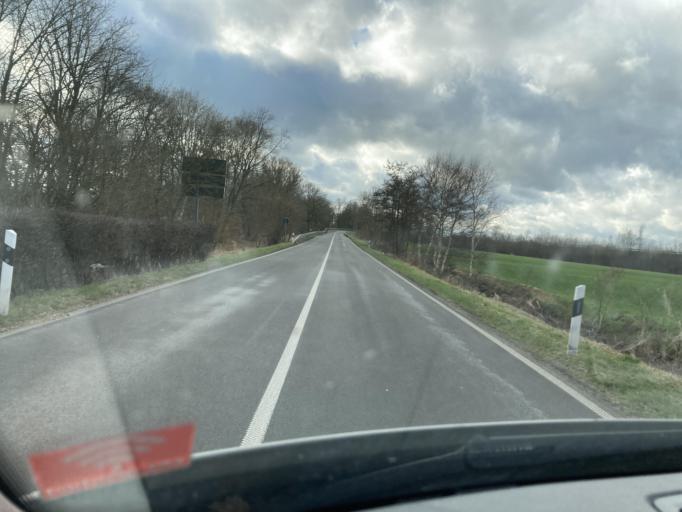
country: DE
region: Lower Saxony
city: Filsum
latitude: 53.2159
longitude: 7.6423
